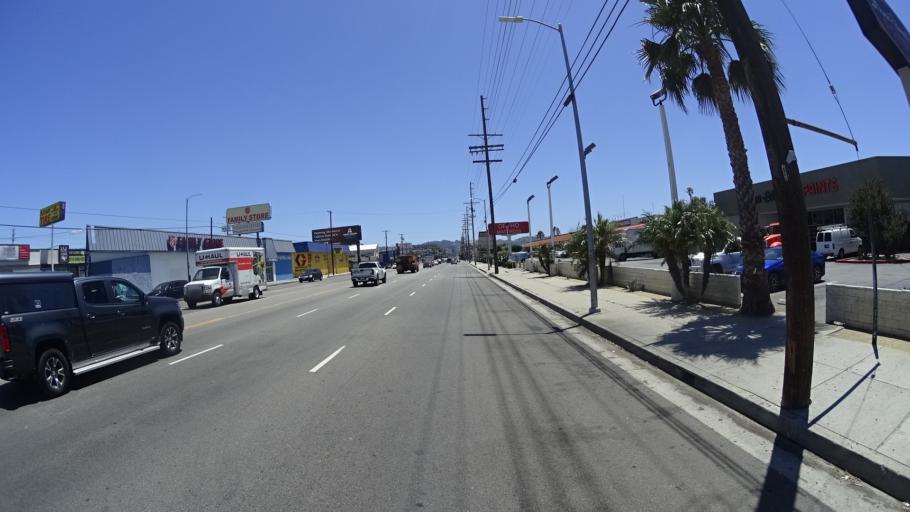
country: US
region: California
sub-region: Los Angeles County
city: Van Nuys
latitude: 34.1854
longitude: -118.4662
